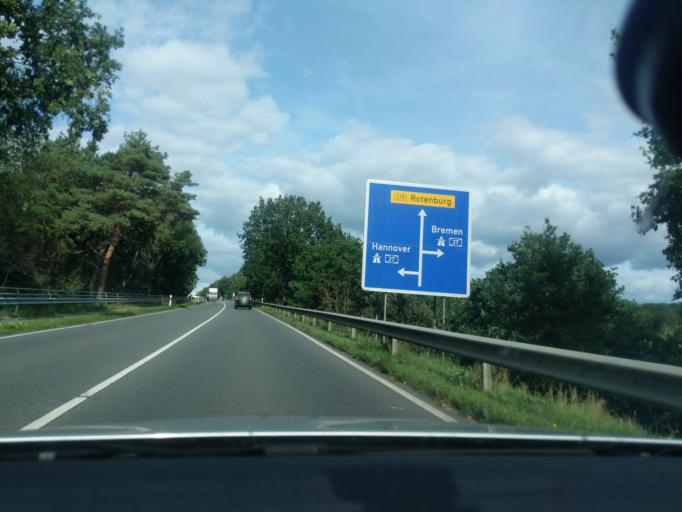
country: DE
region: Lower Saxony
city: Verden
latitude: 52.9563
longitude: 9.2419
